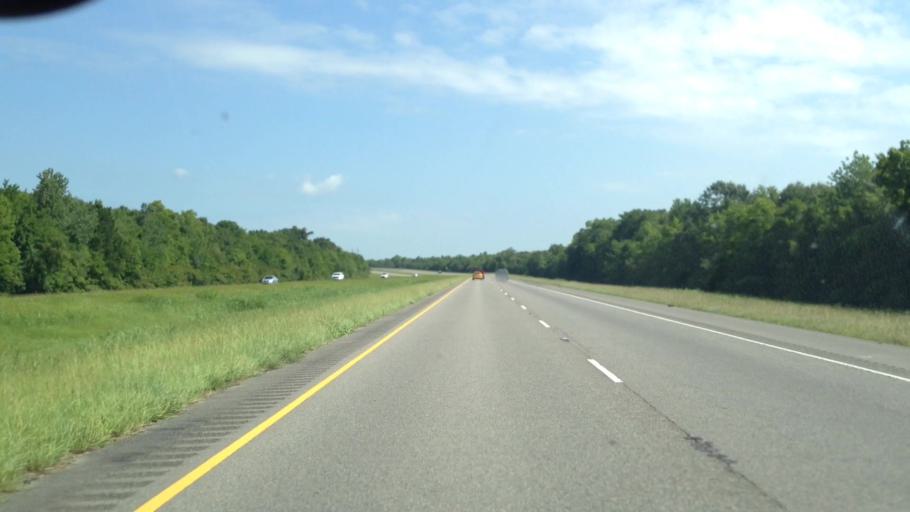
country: US
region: Louisiana
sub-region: Avoyelles Parish
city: Bunkie
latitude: 30.8898
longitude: -92.2269
